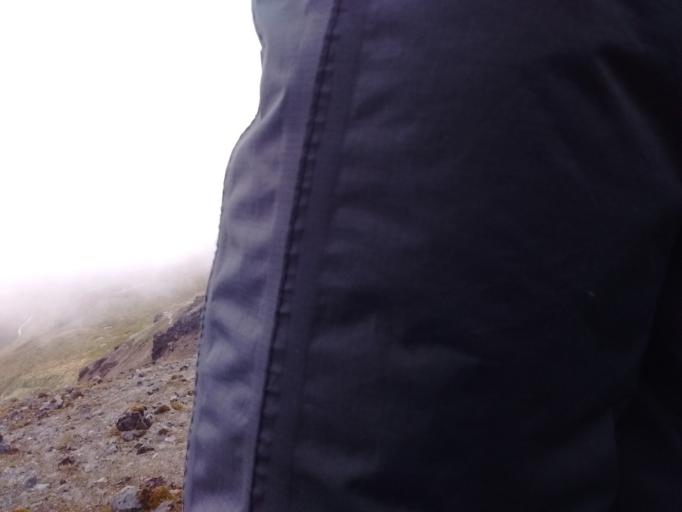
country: CO
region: Cauca
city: Totoro
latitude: 2.3249
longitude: -76.3950
